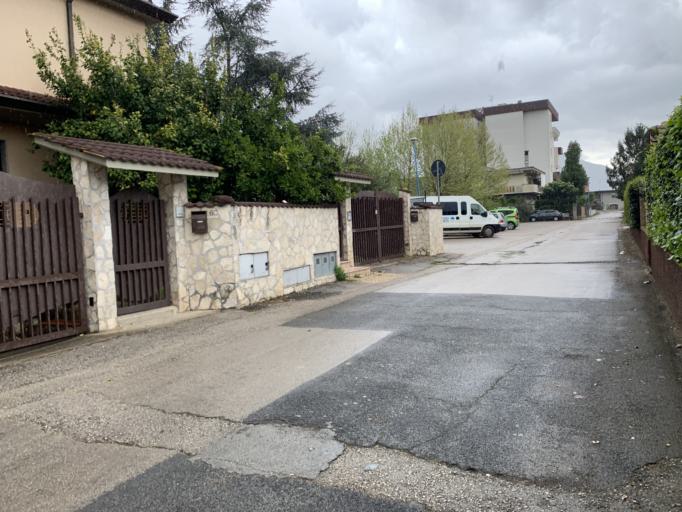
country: IT
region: Latium
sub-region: Provincia di Latina
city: Carrara-Pontenuovo
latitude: 41.5397
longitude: 12.9472
